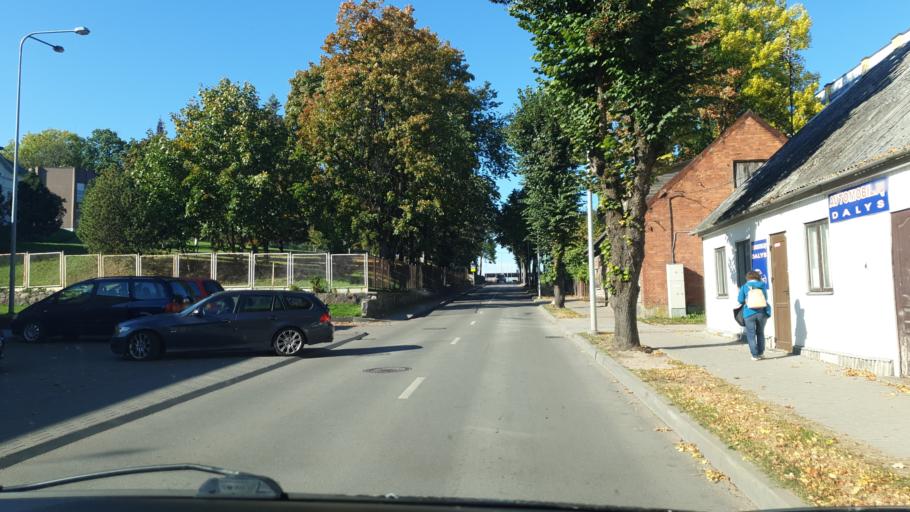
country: LT
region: Telsiu apskritis
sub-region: Telsiai
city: Telsiai
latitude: 55.9839
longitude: 22.2477
